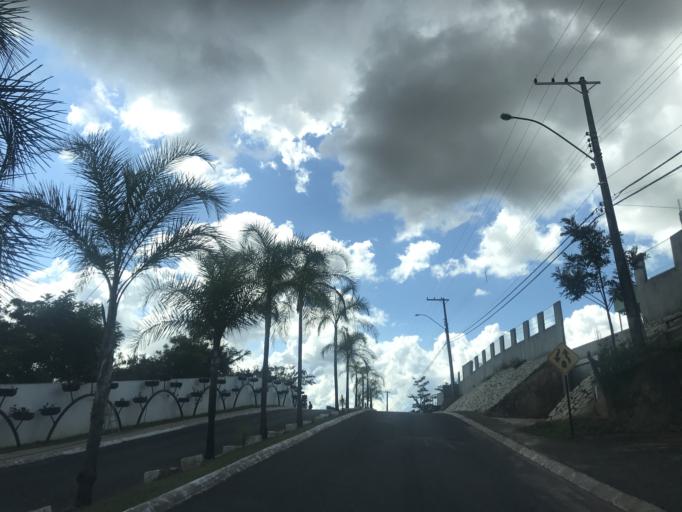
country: BR
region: Federal District
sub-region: Brasilia
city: Brasilia
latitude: -15.8687
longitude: -47.7592
